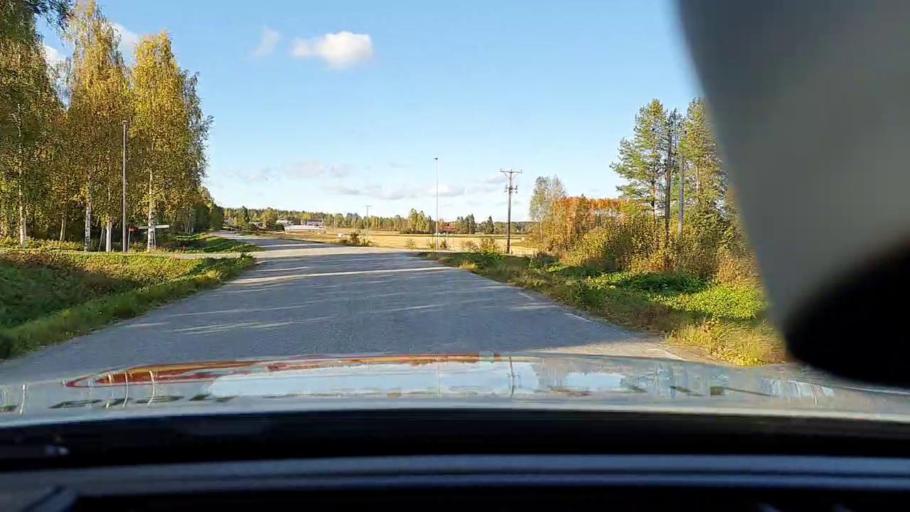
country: SE
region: Norrbotten
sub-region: Pitea Kommun
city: Norrfjarden
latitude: 65.5199
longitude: 21.4948
